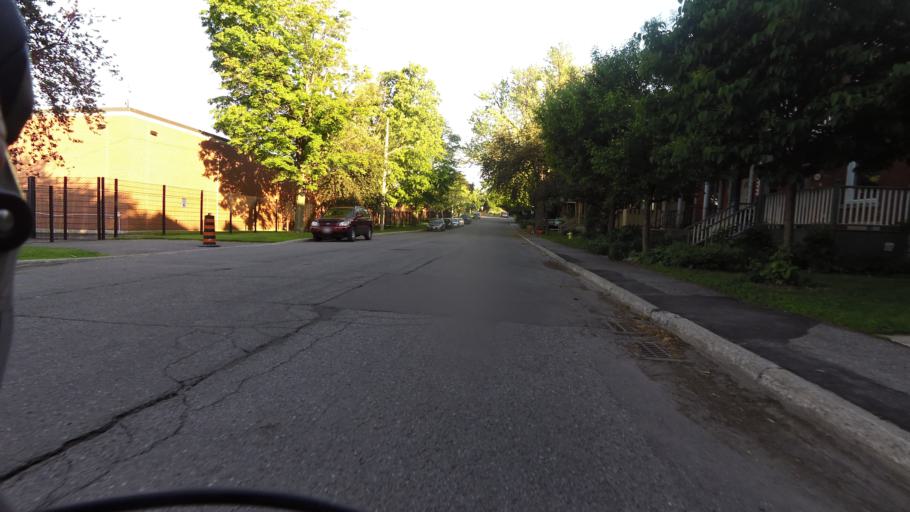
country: CA
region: Ontario
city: Ottawa
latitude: 45.4045
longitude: -75.7179
